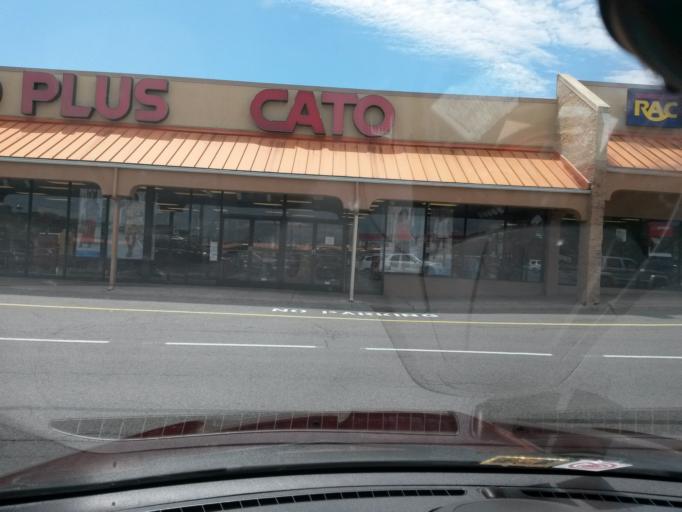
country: US
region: West Virginia
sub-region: Raleigh County
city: Beckley
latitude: 37.8014
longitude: -81.1826
